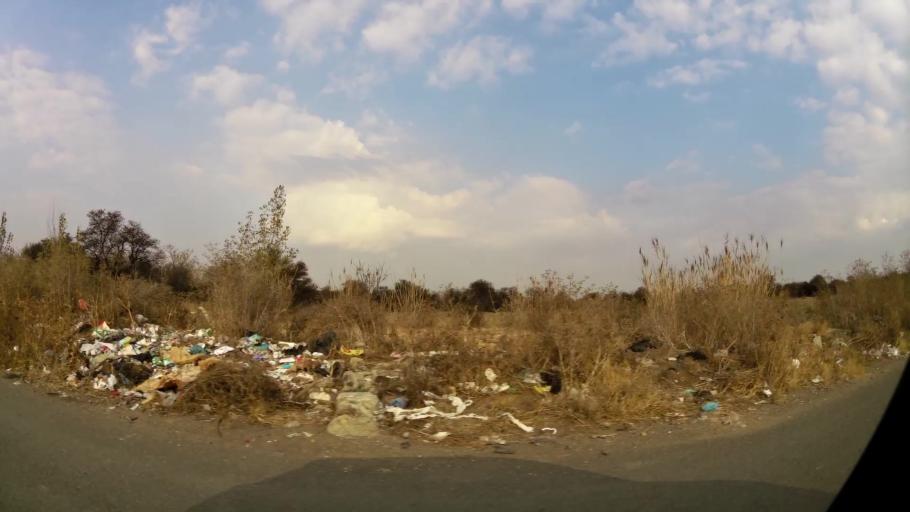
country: ZA
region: Gauteng
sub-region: Sedibeng District Municipality
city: Vereeniging
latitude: -26.6881
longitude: 27.9013
